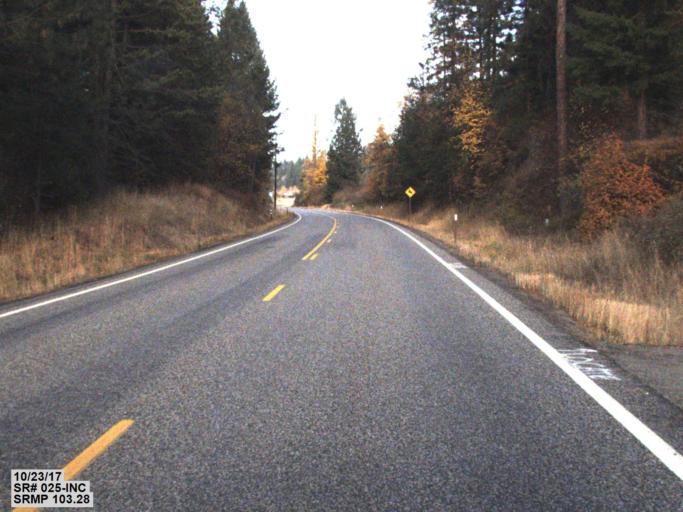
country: US
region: Washington
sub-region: Stevens County
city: Kettle Falls
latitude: 48.8195
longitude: -117.9202
